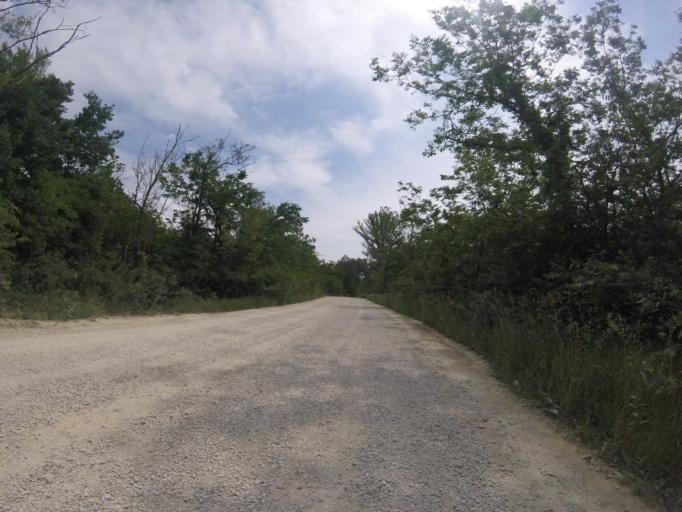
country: HU
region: Pest
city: Leanyfalu
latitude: 47.7192
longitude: 19.1080
